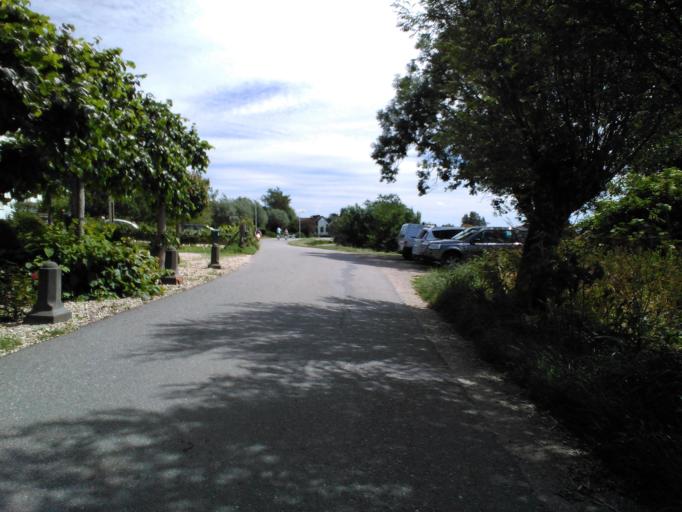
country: NL
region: South Holland
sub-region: Gemeente Sliedrecht
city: Sliedrecht
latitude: 51.8449
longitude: 4.7568
